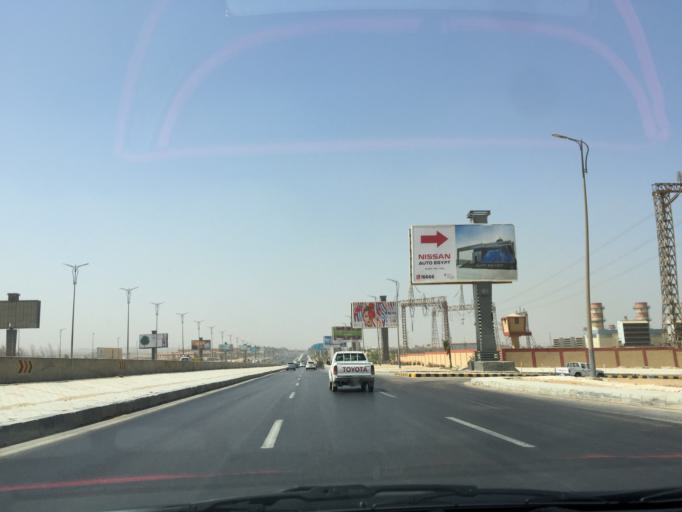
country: EG
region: Al Jizah
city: Awsim
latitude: 30.0504
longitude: 31.0473
